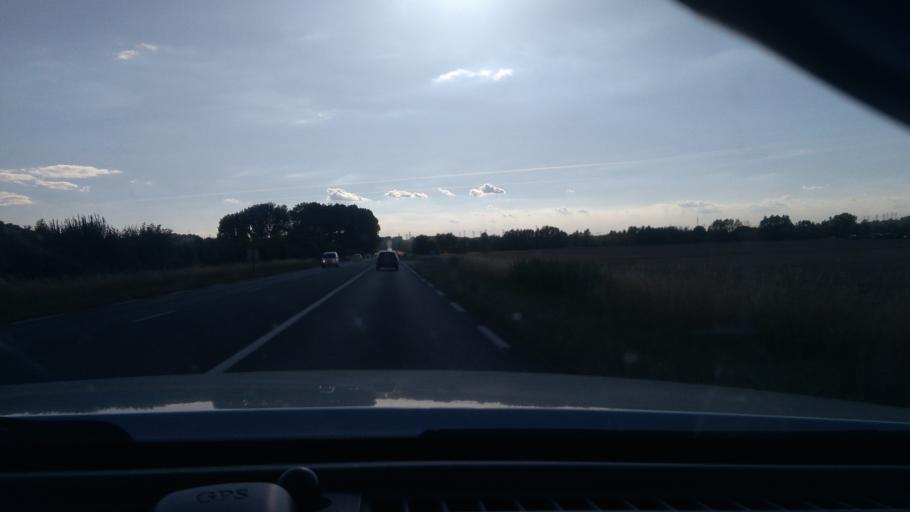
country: FR
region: Ile-de-France
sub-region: Departement de Seine-et-Marne
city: Varennes-sur-Seine
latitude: 48.3612
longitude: 2.9038
